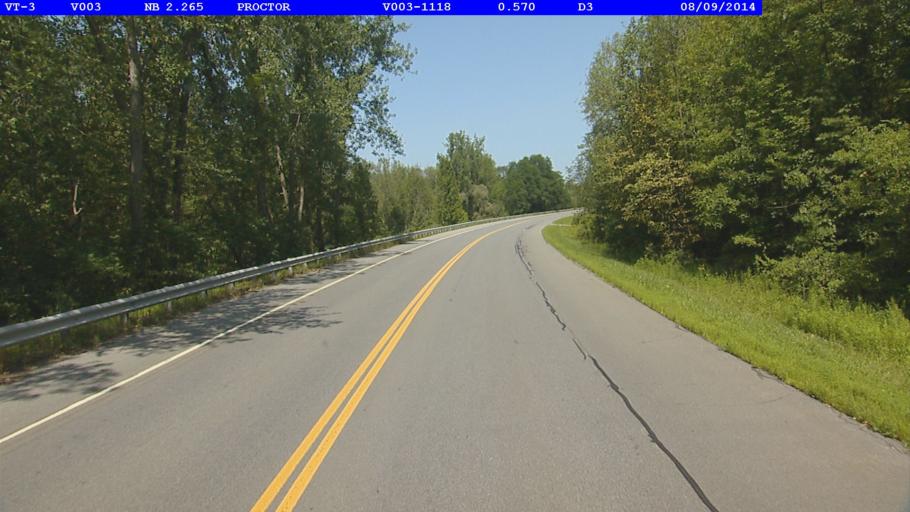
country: US
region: Vermont
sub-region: Rutland County
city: West Rutland
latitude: 43.6323
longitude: -73.0347
